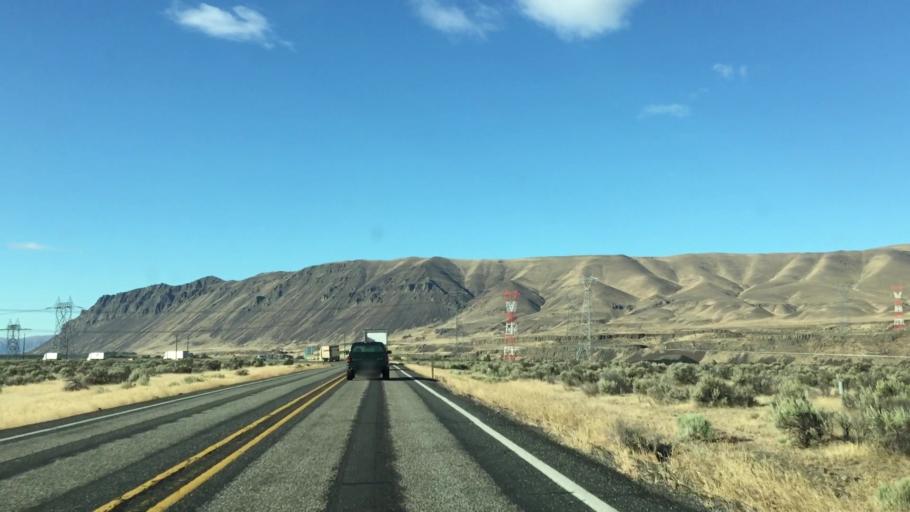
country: US
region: Washington
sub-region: Grant County
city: Mattawa
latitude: 46.8735
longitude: -119.9562
